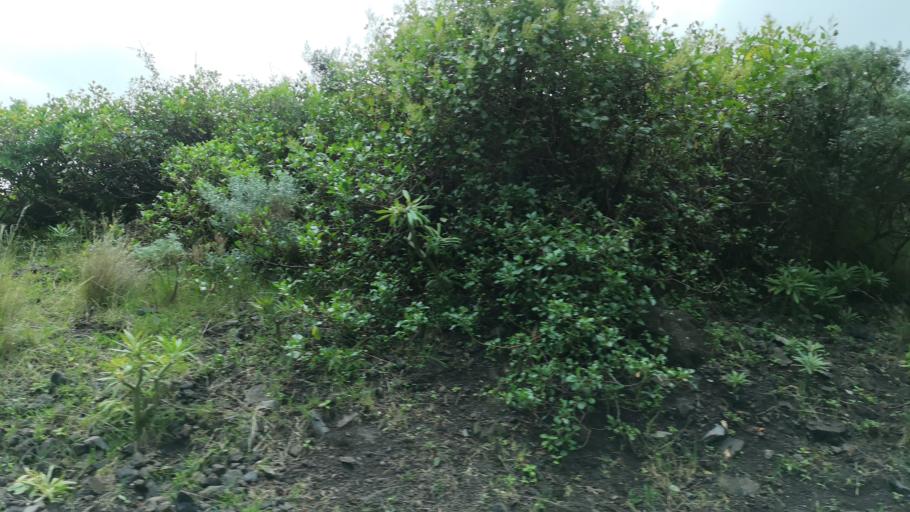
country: ES
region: Canary Islands
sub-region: Provincia de Santa Cruz de Tenerife
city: Hermigua
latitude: 28.1306
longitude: -17.1843
